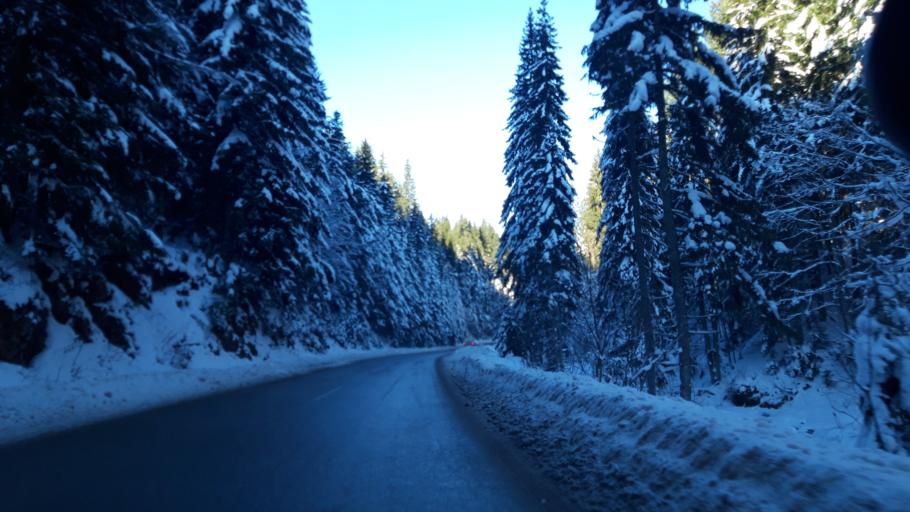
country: BA
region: Republika Srpska
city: Koran
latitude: 43.7492
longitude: 18.5538
